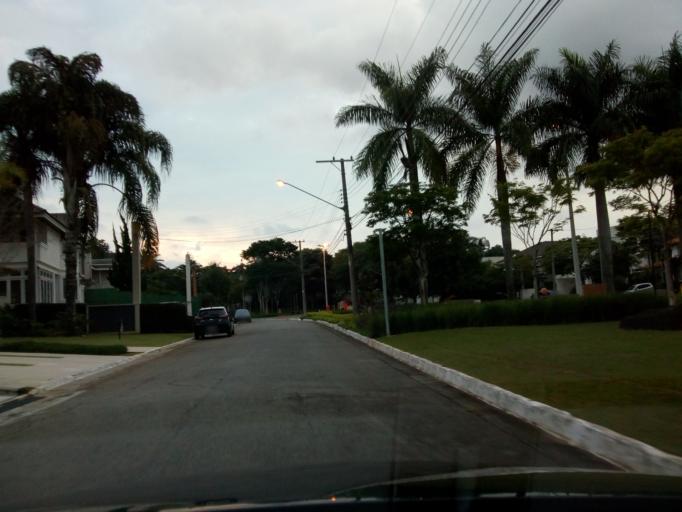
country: BR
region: Sao Paulo
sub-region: Carapicuiba
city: Carapicuiba
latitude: -23.4829
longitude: -46.8369
